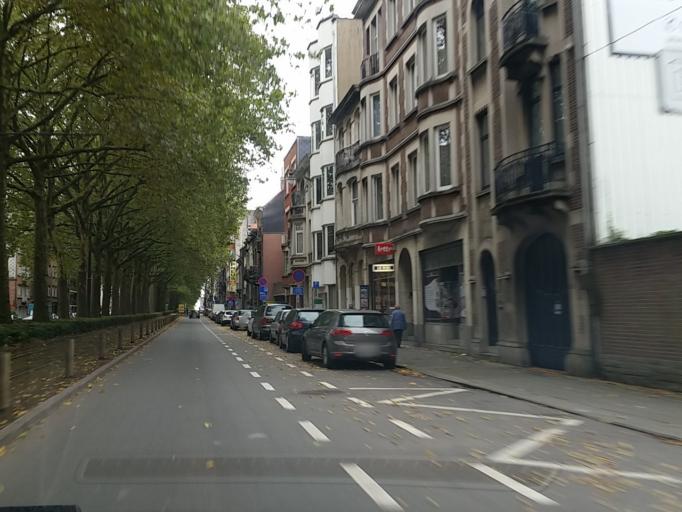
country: BE
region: Flanders
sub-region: Provincie Vlaams-Brabant
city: Drogenbos
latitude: 50.8155
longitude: 4.3252
